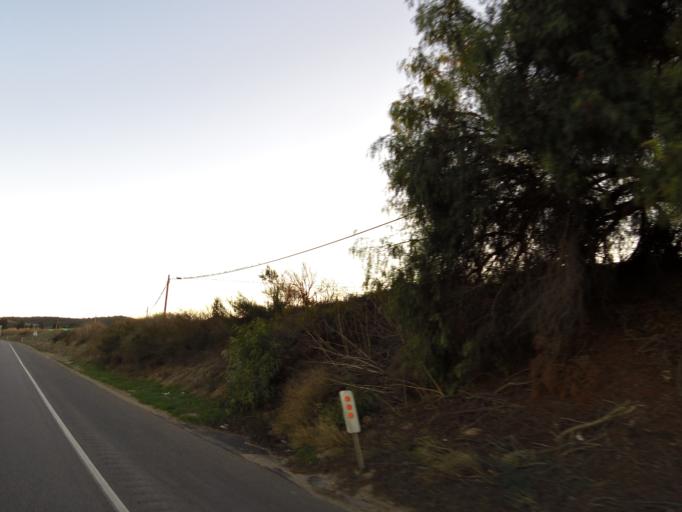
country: US
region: California
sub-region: Monterey County
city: King City
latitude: 36.2323
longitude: -121.1744
